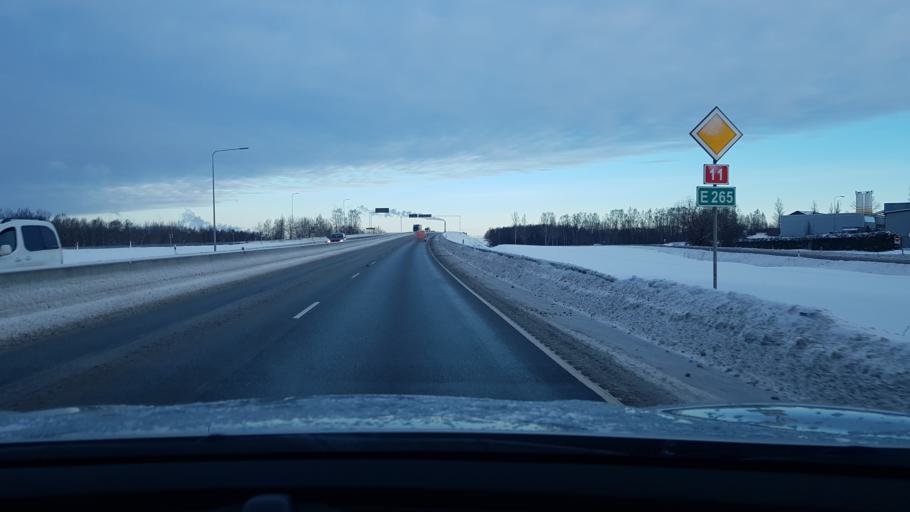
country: EE
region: Harju
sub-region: Joelaehtme vald
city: Loo
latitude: 59.4028
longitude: 24.9157
